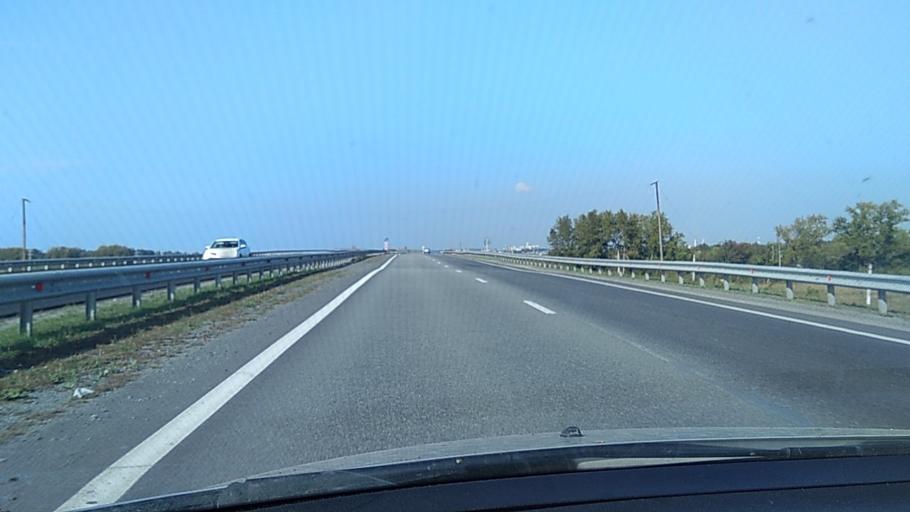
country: RU
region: Chelyabinsk
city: Sargazy
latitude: 55.0497
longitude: 61.3058
